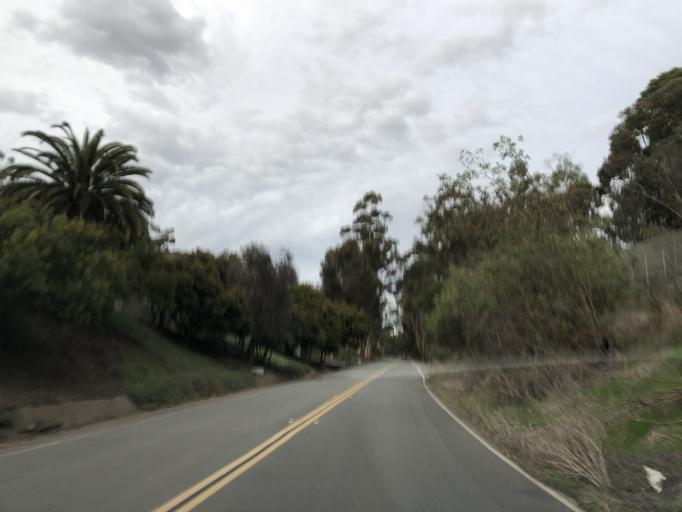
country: US
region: California
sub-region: San Diego County
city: San Diego
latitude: 32.7376
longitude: -117.1544
